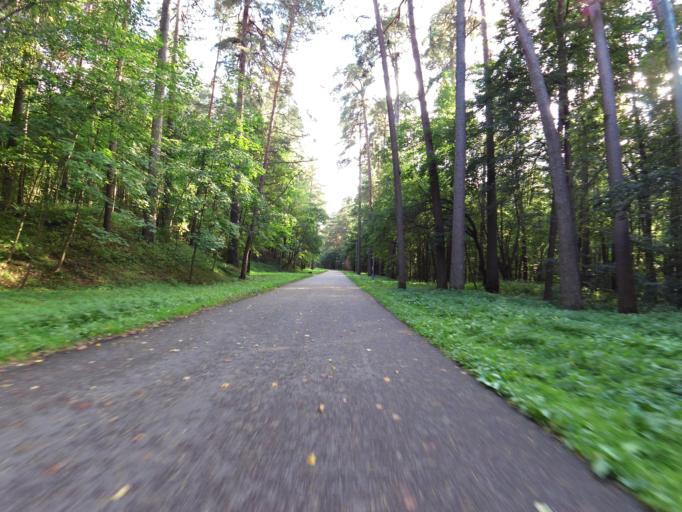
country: LT
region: Vilnius County
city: Vilkpede
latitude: 54.6816
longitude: 25.2415
